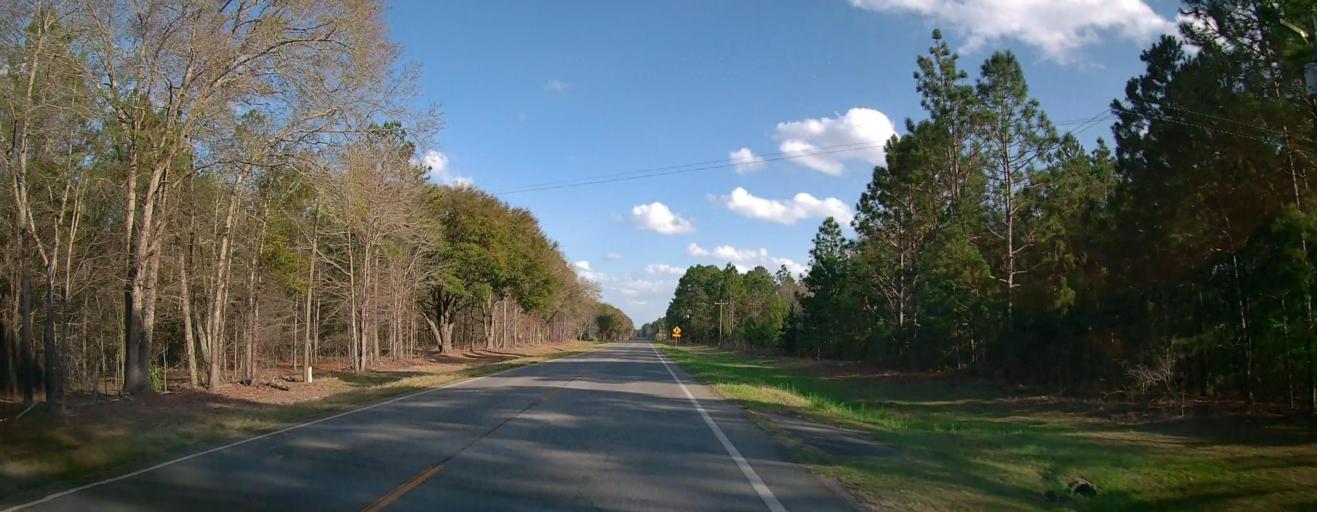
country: US
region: Georgia
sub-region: Toombs County
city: Lyons
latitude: 32.1825
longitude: -82.2946
